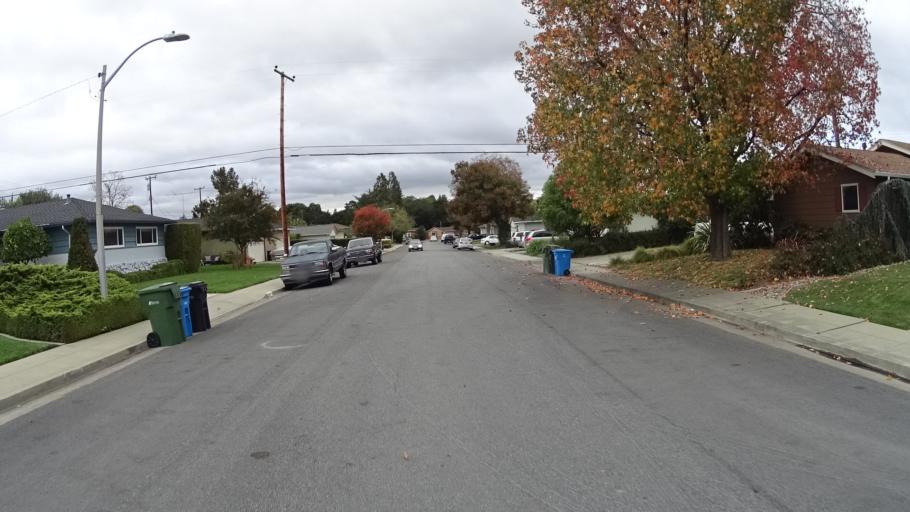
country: US
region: California
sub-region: Santa Clara County
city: Santa Clara
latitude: 37.3354
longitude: -121.9857
